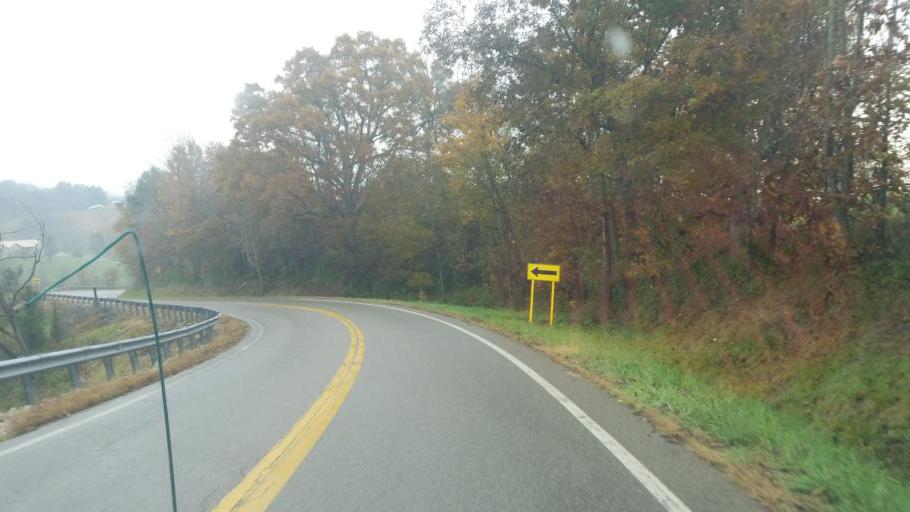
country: US
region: Ohio
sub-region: Morgan County
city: McConnelsville
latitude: 39.4770
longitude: -81.8747
